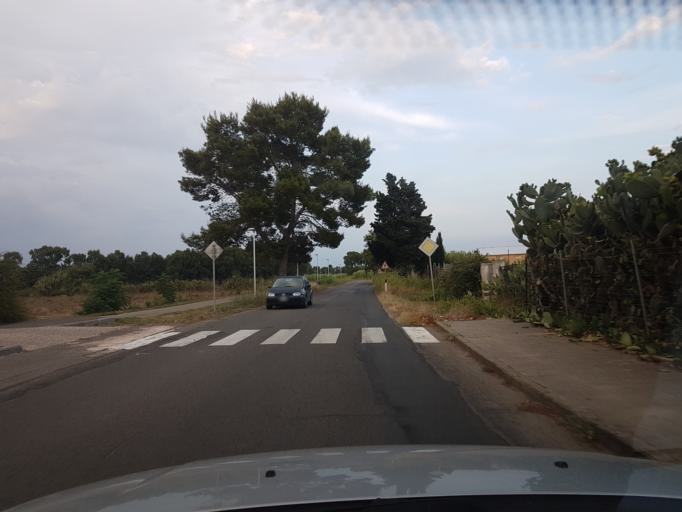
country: IT
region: Sardinia
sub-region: Provincia di Oristano
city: Cabras
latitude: 39.9293
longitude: 8.5400
